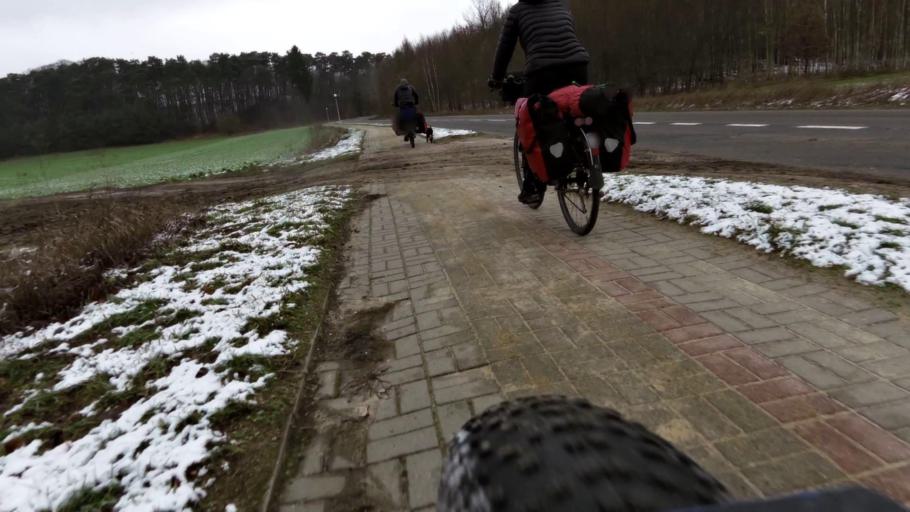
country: PL
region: West Pomeranian Voivodeship
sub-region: Powiat walecki
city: Miroslawiec
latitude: 53.3548
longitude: 16.0855
